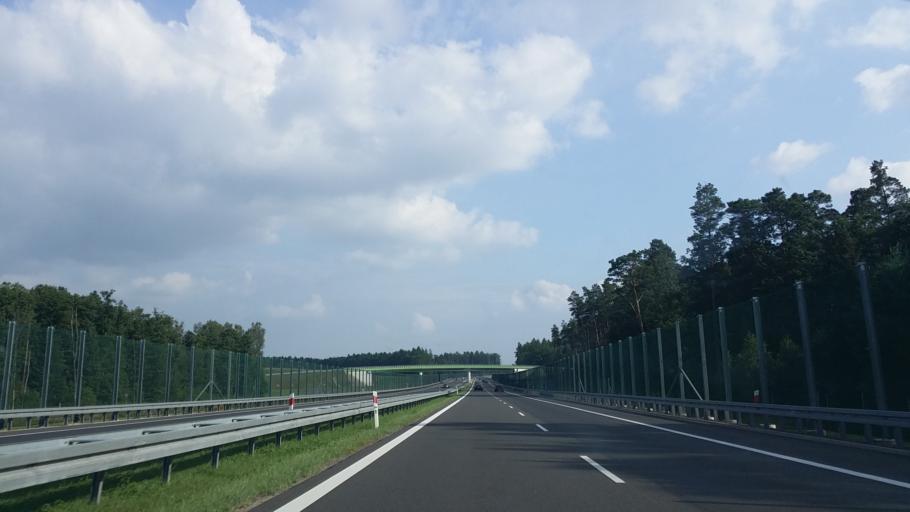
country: PL
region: Lubusz
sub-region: Powiat miedzyrzecki
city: Miedzyrzecz
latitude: 52.5126
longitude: 15.5495
